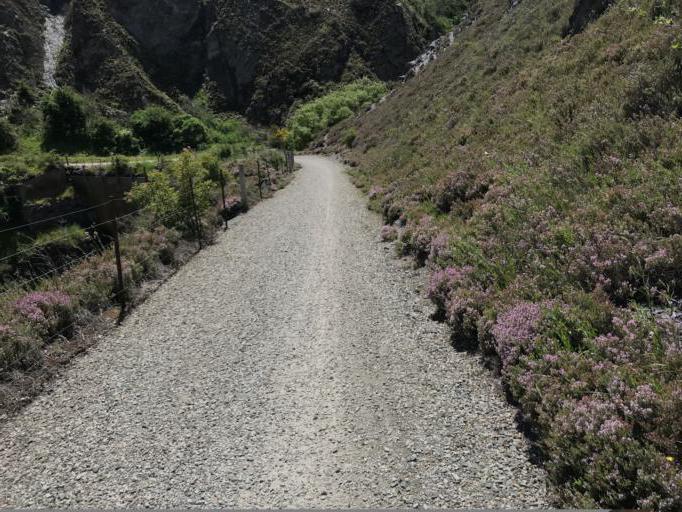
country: NZ
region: Otago
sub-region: Queenstown-Lakes District
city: Arrowtown
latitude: -45.0048
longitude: 168.8812
